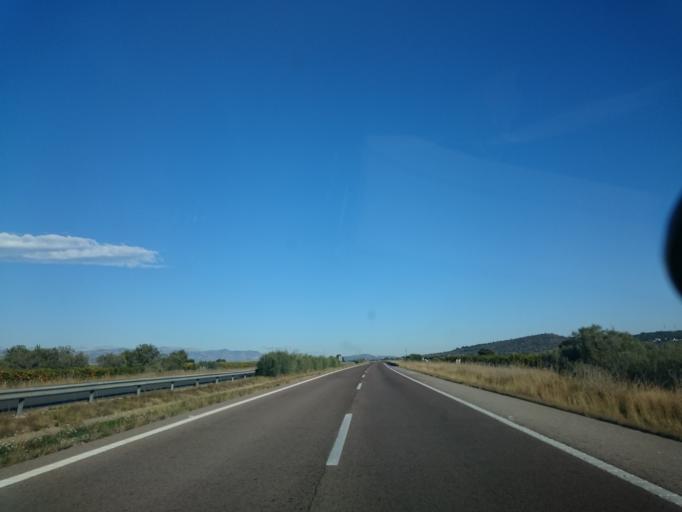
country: ES
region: Valencia
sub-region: Provincia de Castello
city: Vinaros
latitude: 40.4945
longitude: 0.4153
